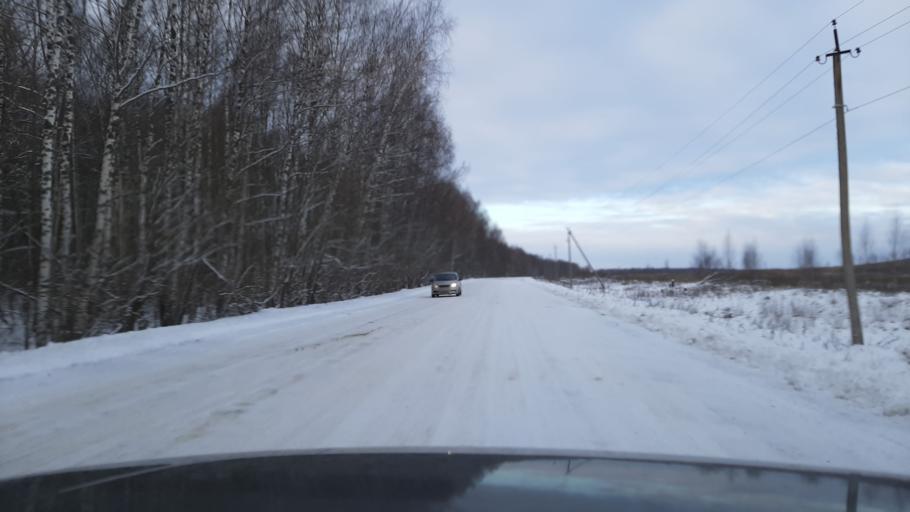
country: RU
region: Kostroma
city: Nerekhta
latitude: 57.4704
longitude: 40.6854
